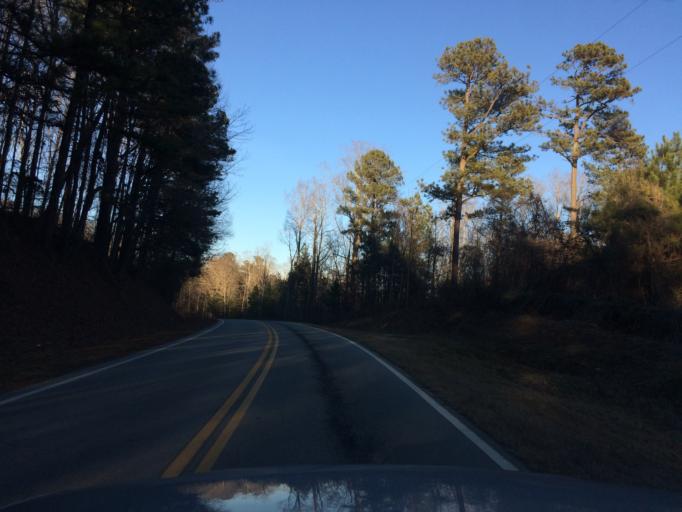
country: US
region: Georgia
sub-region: Barrow County
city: Winder
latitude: 33.9736
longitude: -83.7695
